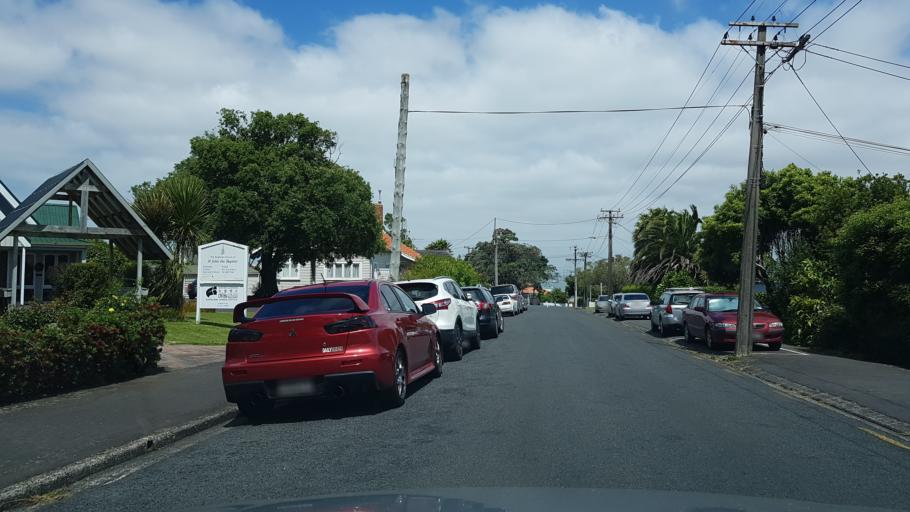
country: NZ
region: Auckland
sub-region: Auckland
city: North Shore
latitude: -36.8115
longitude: 174.7420
